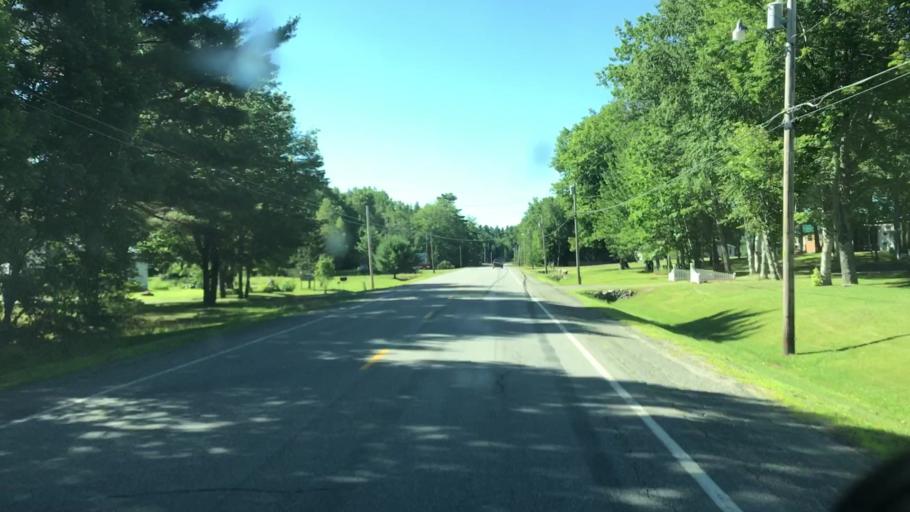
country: US
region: Maine
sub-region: Penobscot County
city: Howland
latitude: 45.2592
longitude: -68.6380
